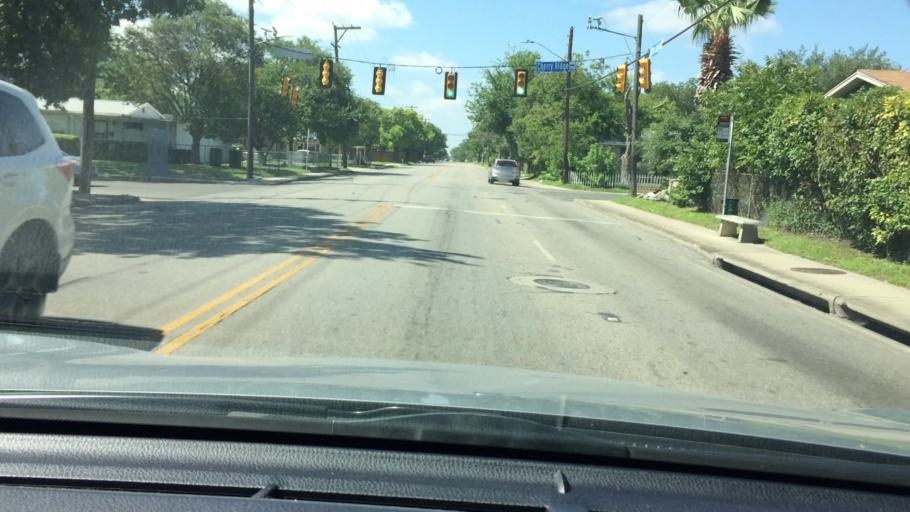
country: US
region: Texas
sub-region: Bexar County
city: Castle Hills
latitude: 29.5075
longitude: -98.5352
